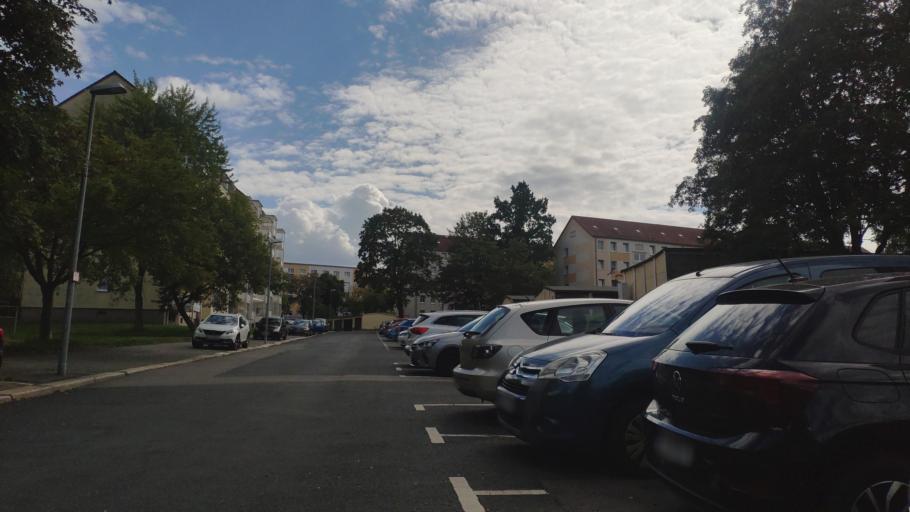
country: DE
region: Saxony
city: Chemnitz
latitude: 50.8230
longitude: 12.9047
